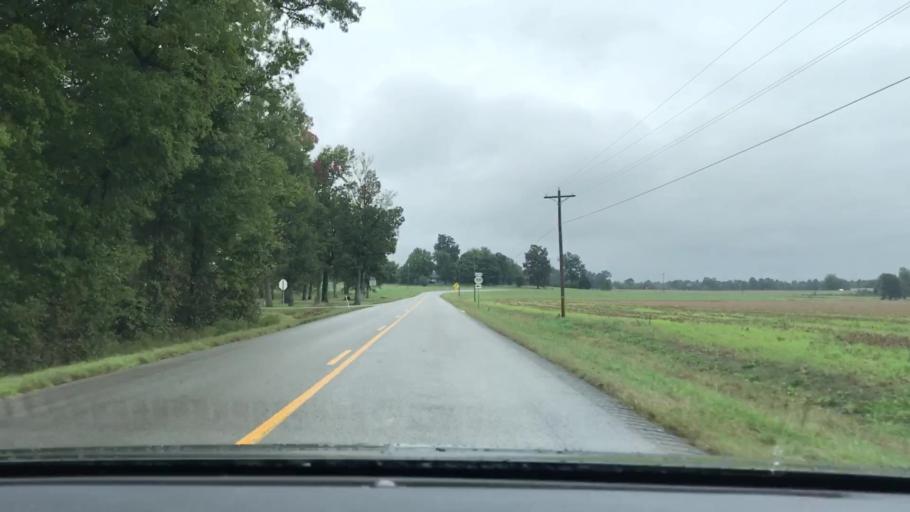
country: US
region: Kentucky
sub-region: McLean County
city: Calhoun
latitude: 37.4717
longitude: -87.2370
